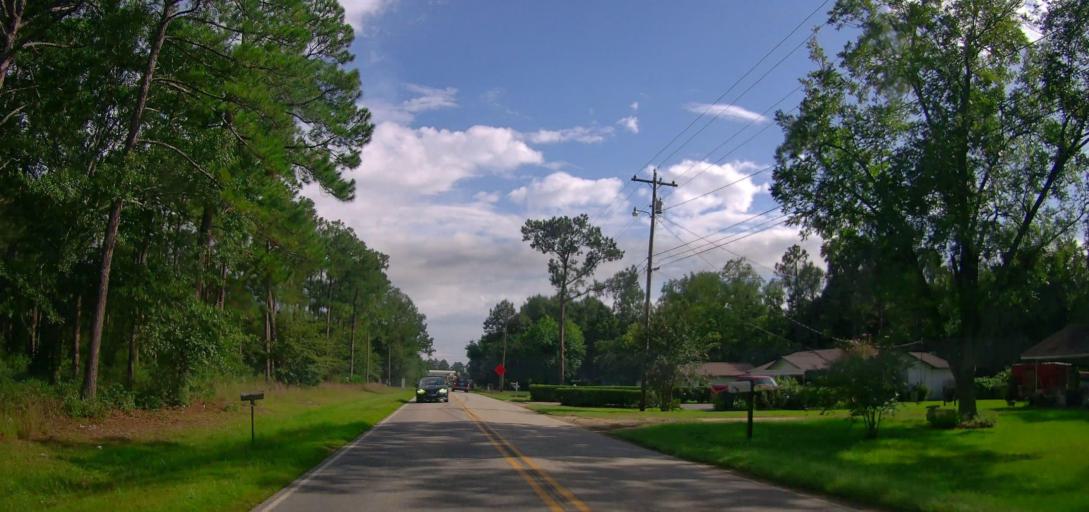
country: US
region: Georgia
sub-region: Coffee County
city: Douglas
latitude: 31.4908
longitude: -82.8589
